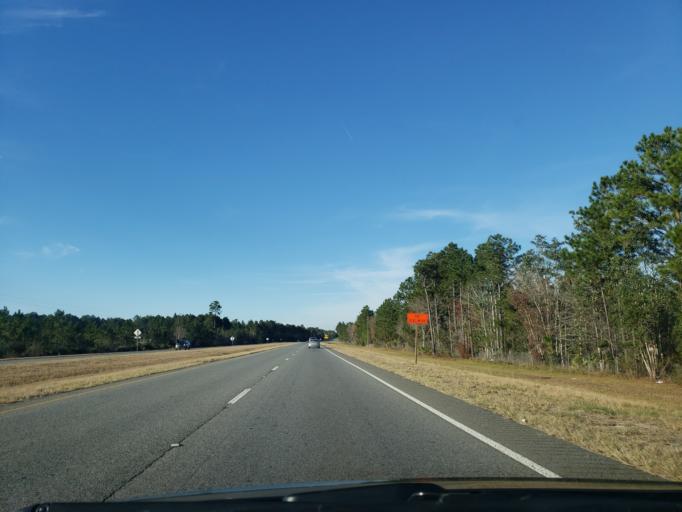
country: US
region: Georgia
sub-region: Ware County
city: Deenwood
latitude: 31.2243
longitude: -82.4248
